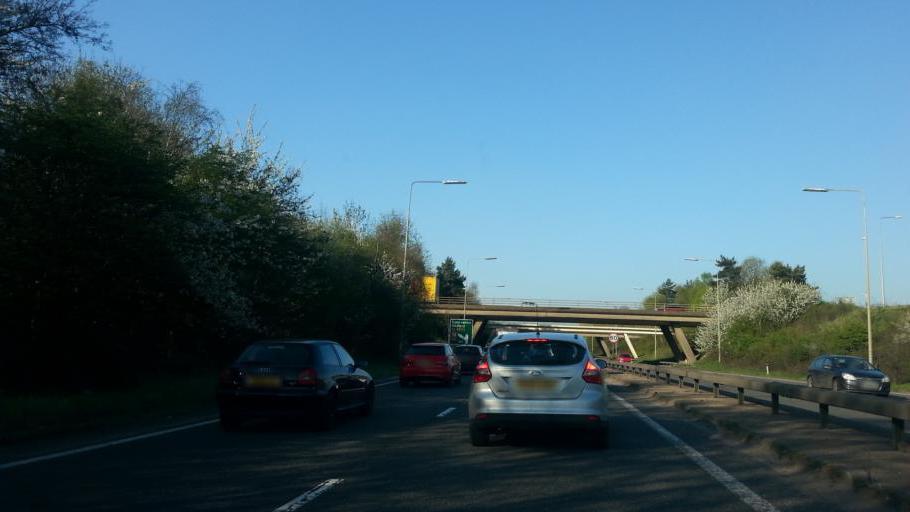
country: GB
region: England
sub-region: Northamptonshire
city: Hardingstone
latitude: 52.2205
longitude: -0.8774
